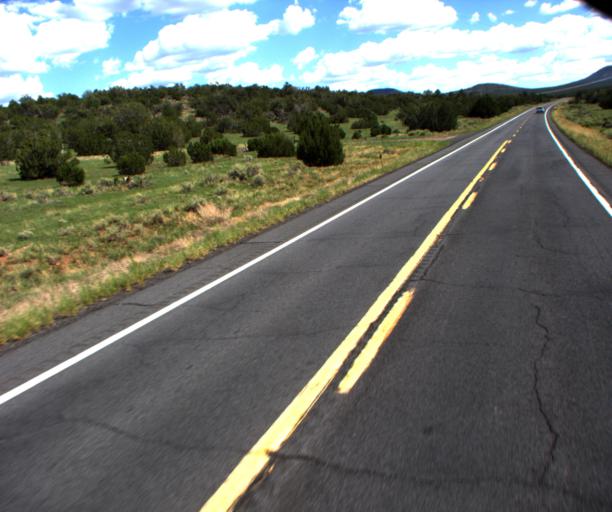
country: US
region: Arizona
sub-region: Coconino County
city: Williams
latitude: 35.4681
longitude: -112.1738
